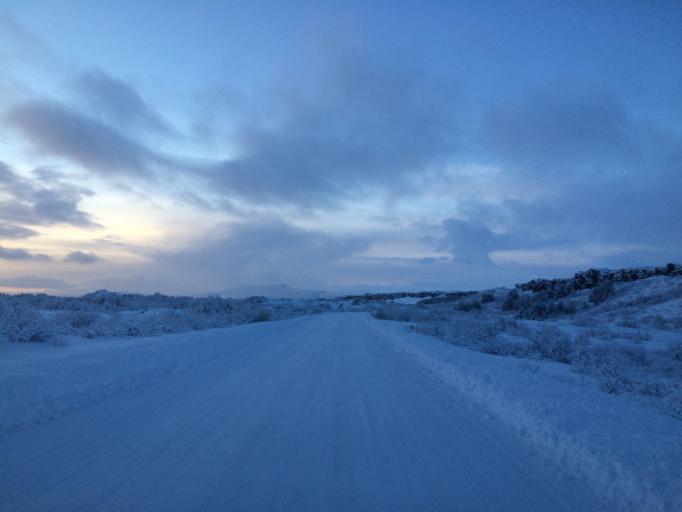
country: IS
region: South
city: Hveragerdi
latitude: 64.2752
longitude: -21.0973
